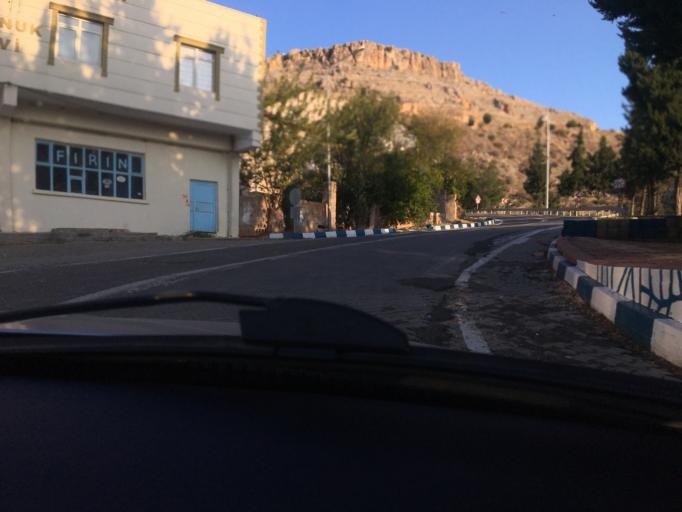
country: TR
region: Sanliurfa
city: Halfeti
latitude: 37.2440
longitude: 37.8714
